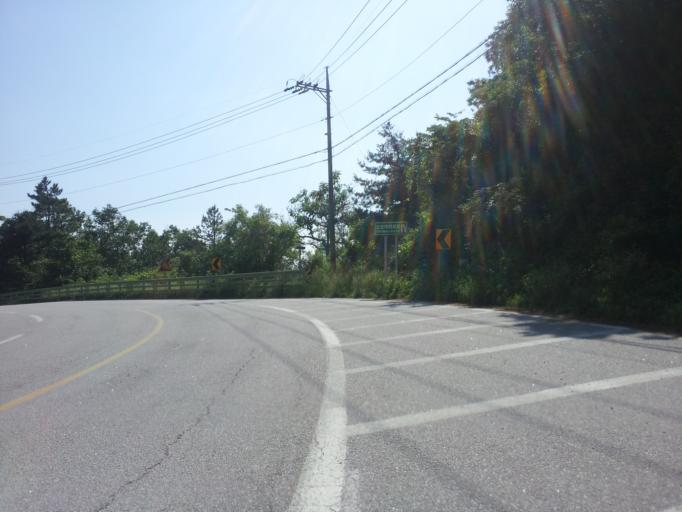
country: KR
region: Chungcheongbuk-do
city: Okcheon
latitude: 36.4787
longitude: 127.6428
